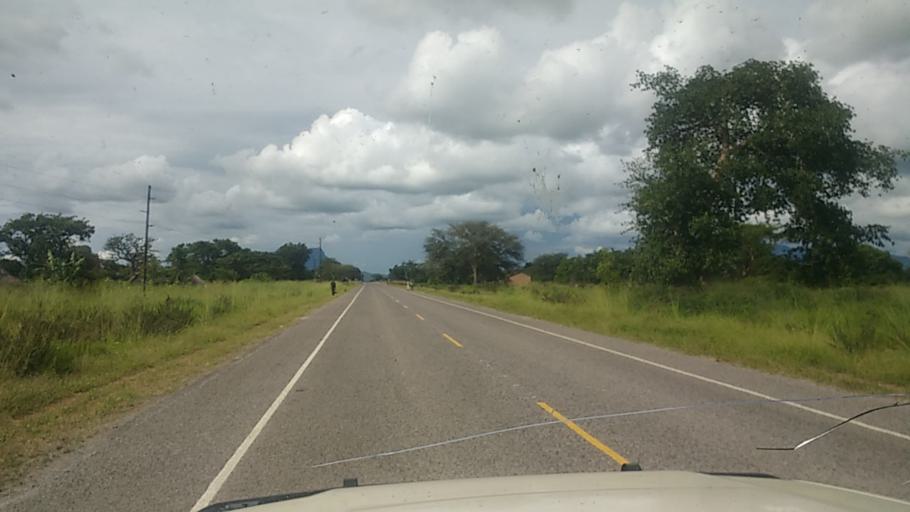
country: UG
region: Eastern Region
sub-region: Katakwi District
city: Katakwi
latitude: 2.0194
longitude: 34.1130
